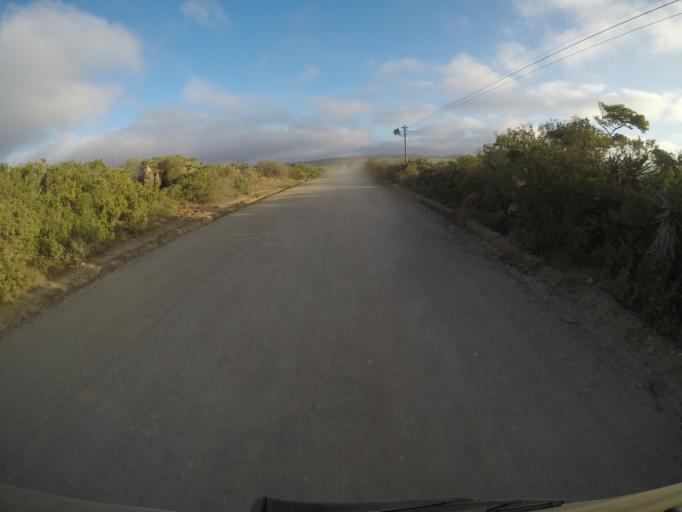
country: ZA
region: Western Cape
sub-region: Eden District Municipality
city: Mossel Bay
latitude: -34.1138
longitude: 22.0533
